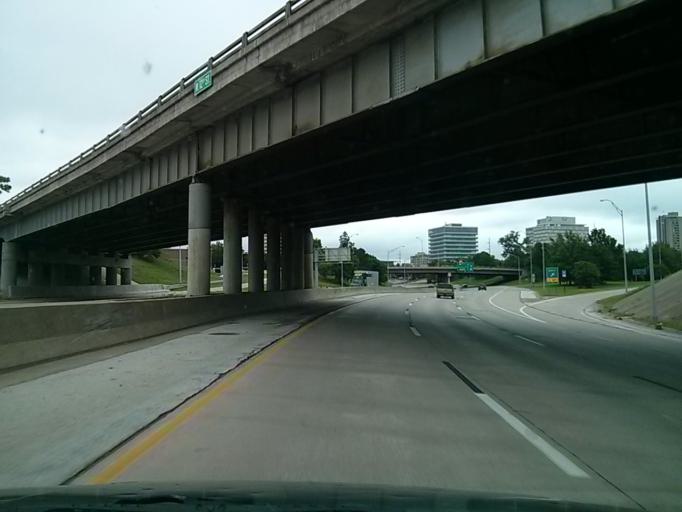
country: US
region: Oklahoma
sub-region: Tulsa County
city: Tulsa
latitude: 36.1453
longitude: -95.9953
